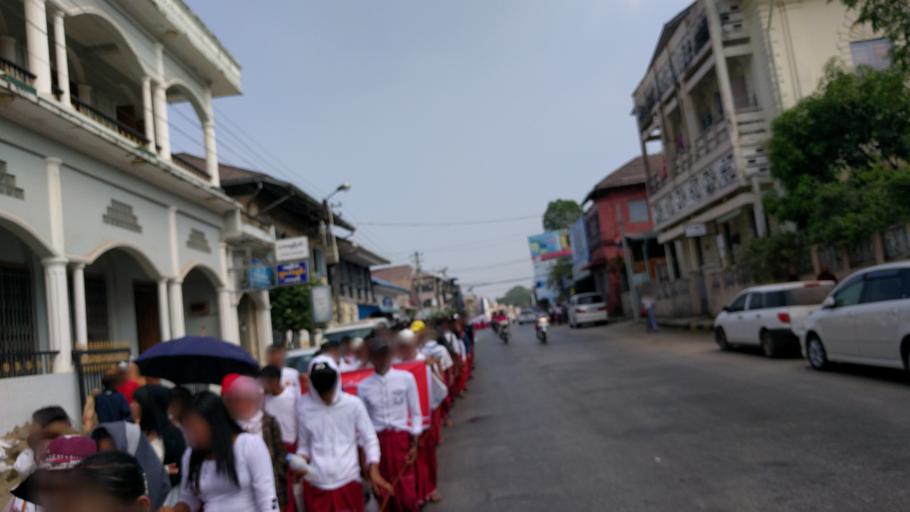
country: MM
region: Mon
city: Mawlamyine
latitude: 16.4799
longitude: 97.6198
